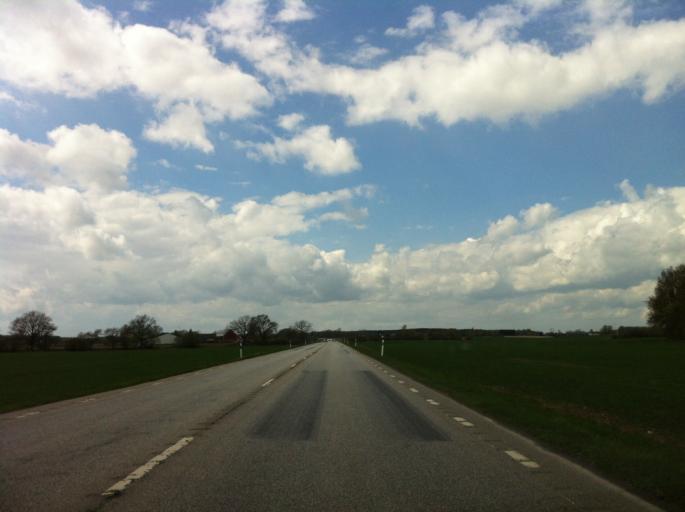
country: SE
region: Skane
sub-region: Eslovs Kommun
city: Stehag
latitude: 55.8480
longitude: 13.4337
